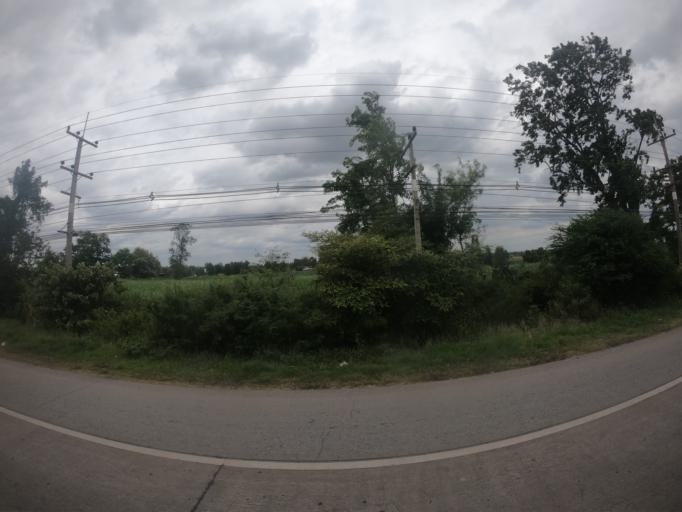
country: TH
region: Nakhon Ratchasima
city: Chok Chai
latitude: 14.7939
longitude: 102.1688
